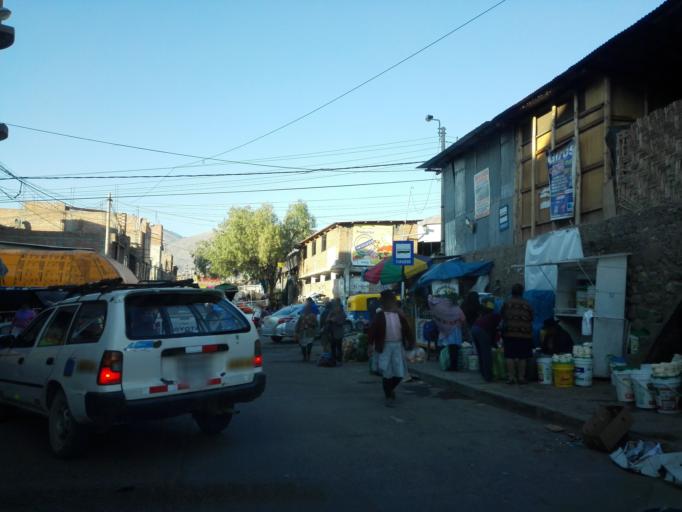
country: PE
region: Ayacucho
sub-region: Provincia de Huamanga
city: Ayacucho
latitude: -13.1490
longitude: -74.2294
